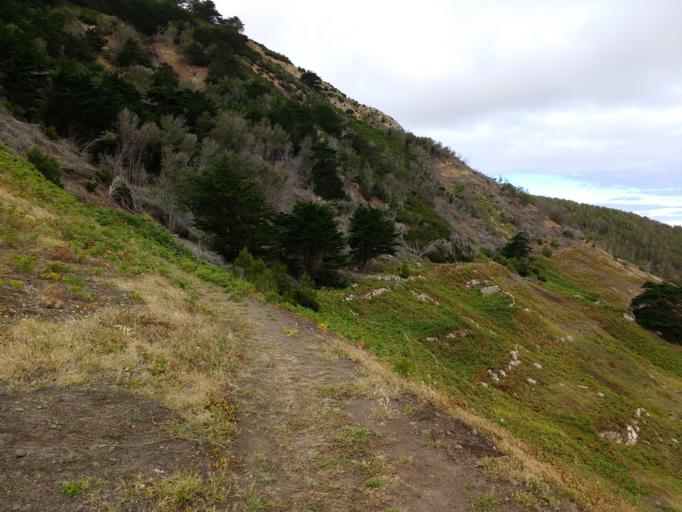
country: PT
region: Madeira
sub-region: Porto Santo
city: Camacha
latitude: 33.0852
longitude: -16.3188
